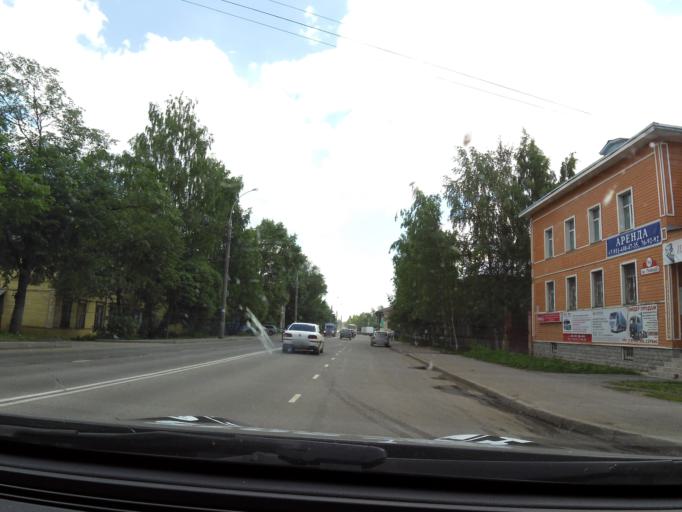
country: RU
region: Vologda
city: Vologda
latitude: 59.2247
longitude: 39.8715
